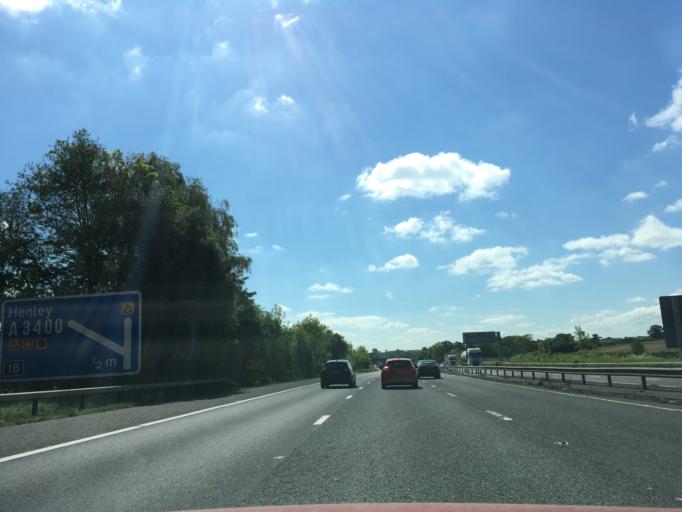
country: GB
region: England
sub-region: Solihull
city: Cheswick Green
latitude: 52.3422
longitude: -1.7898
